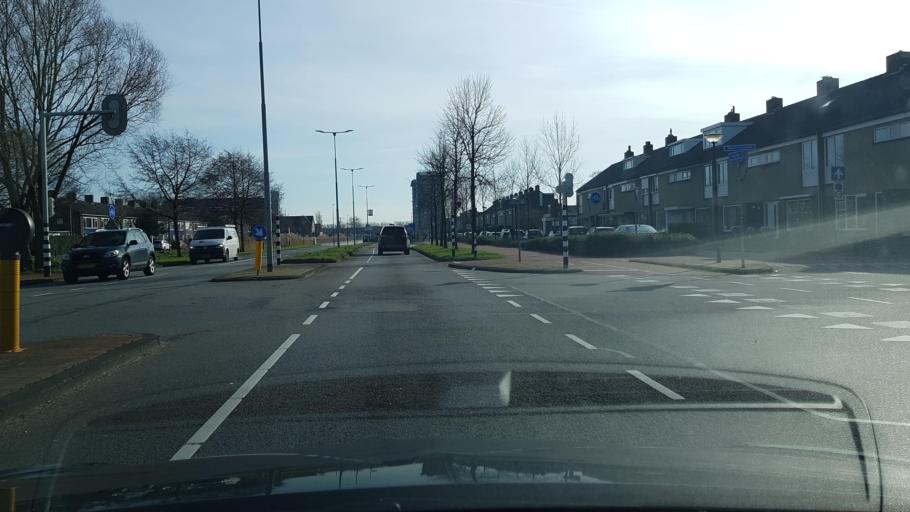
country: NL
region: North Holland
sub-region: Gemeente Beverwijk
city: Beverwijk
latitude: 52.4912
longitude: 4.6744
